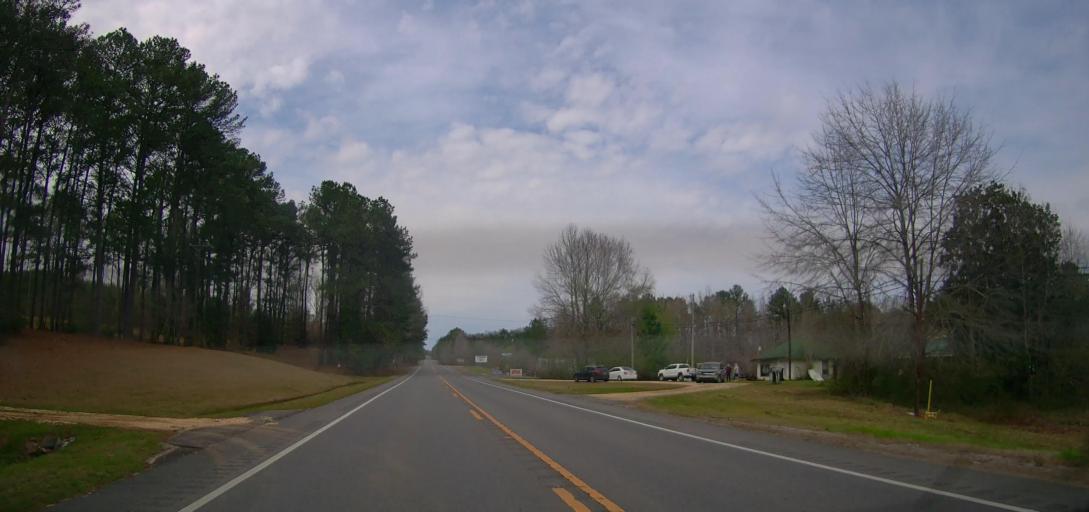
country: US
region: Alabama
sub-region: Marion County
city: Guin
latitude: 34.0084
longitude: -87.9343
